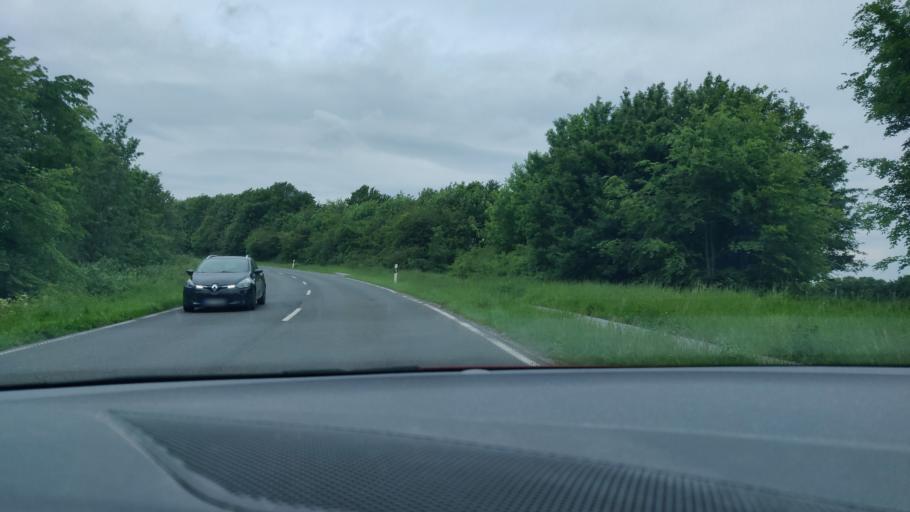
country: DE
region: North Rhine-Westphalia
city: Wulfrath
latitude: 51.2989
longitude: 7.0735
